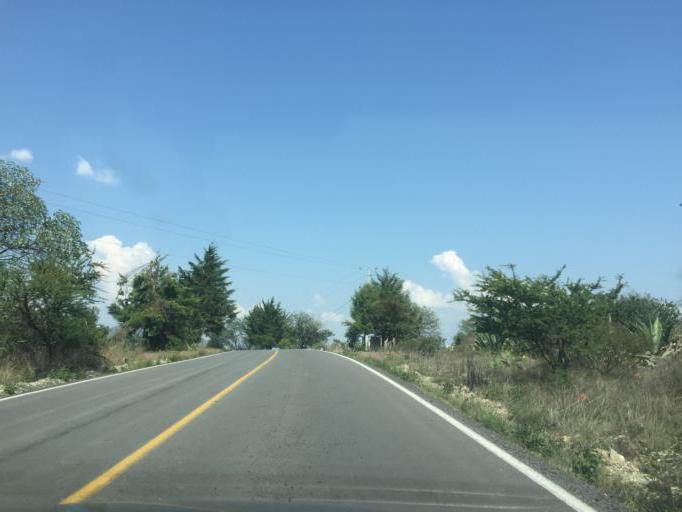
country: MX
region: Hidalgo
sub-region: Cardonal
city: Pozuelos
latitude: 20.6143
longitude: -99.0574
